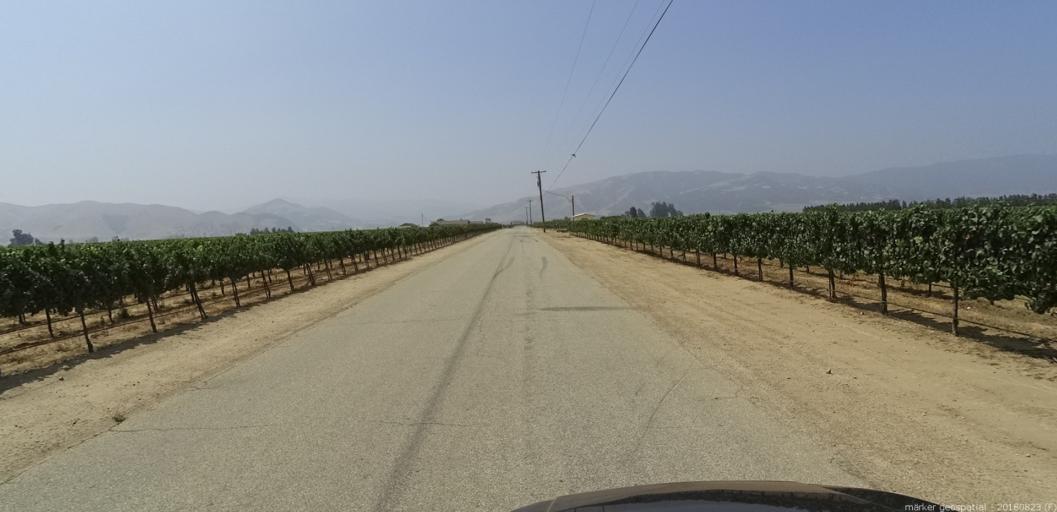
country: US
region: California
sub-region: Monterey County
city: Greenfield
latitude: 36.3240
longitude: -121.2692
